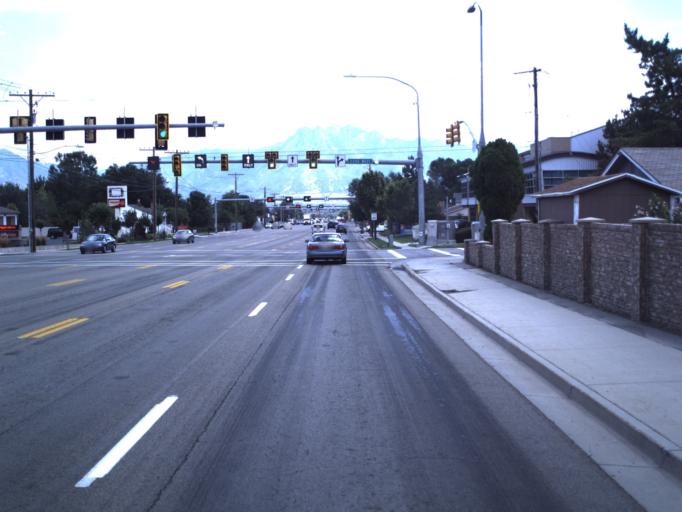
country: US
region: Utah
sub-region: Salt Lake County
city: Taylorsville
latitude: 40.6530
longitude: -111.9490
